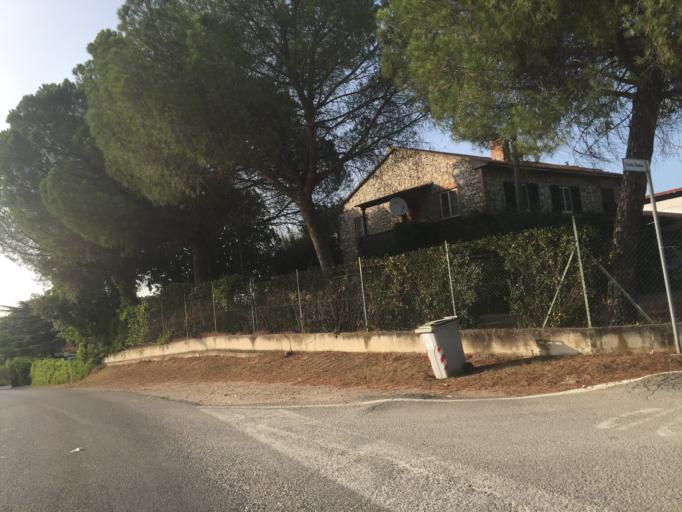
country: IT
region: Umbria
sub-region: Provincia di Perugia
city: Torgiano
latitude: 43.0293
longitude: 12.4297
